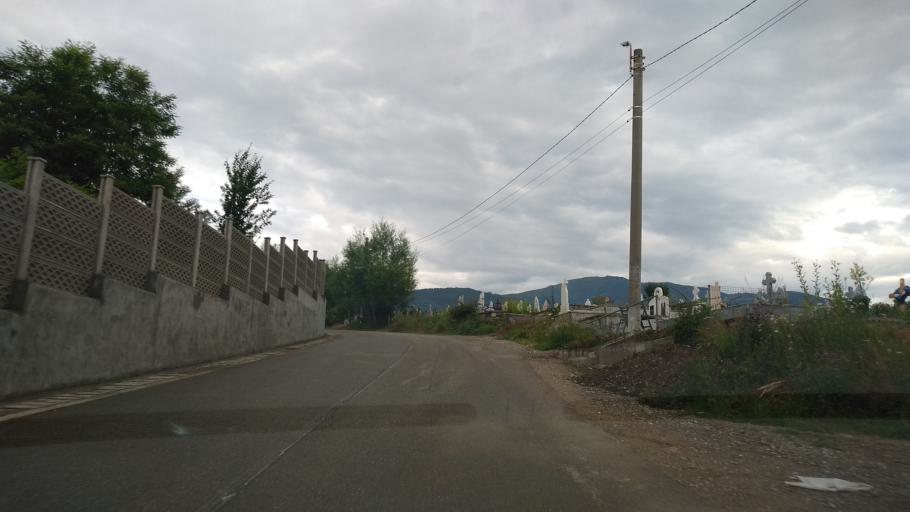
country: RO
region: Hunedoara
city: Vulcan
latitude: 45.3684
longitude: 23.2828
